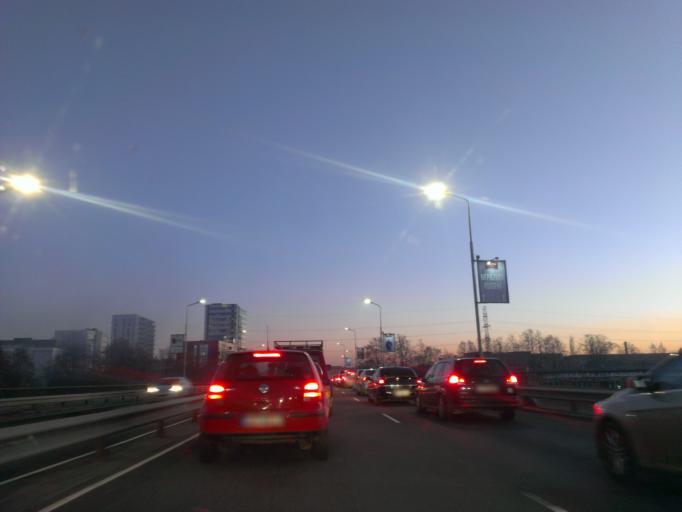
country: LV
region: Riga
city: Jaunciems
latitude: 56.9801
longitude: 24.1626
